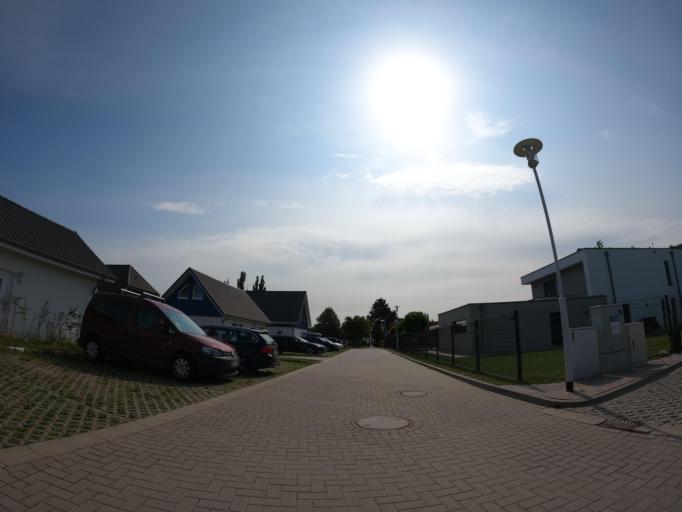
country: DE
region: Mecklenburg-Vorpommern
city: Altefahr
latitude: 54.3324
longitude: 13.1238
